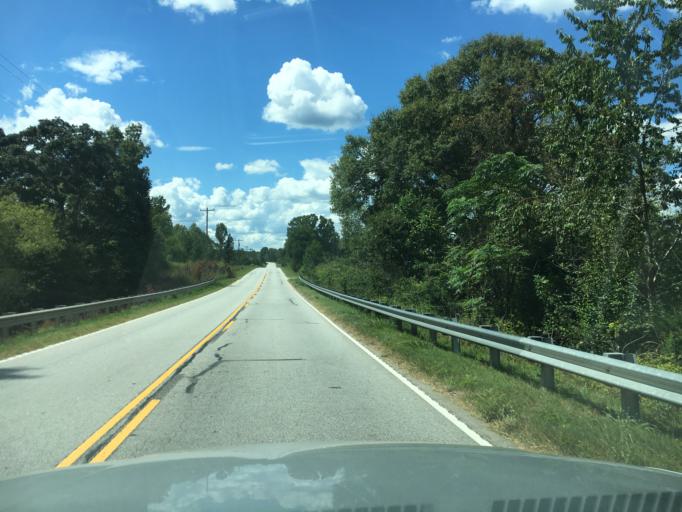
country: US
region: South Carolina
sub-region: Greenwood County
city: Ware Shoals
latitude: 34.5208
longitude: -82.1720
